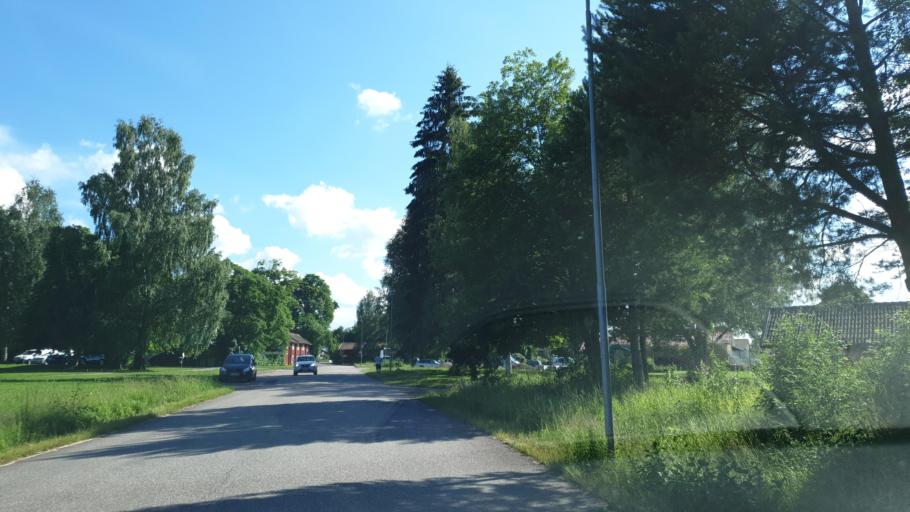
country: SE
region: Dalarna
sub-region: Avesta Kommun
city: Avesta
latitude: 60.1258
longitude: 16.2523
